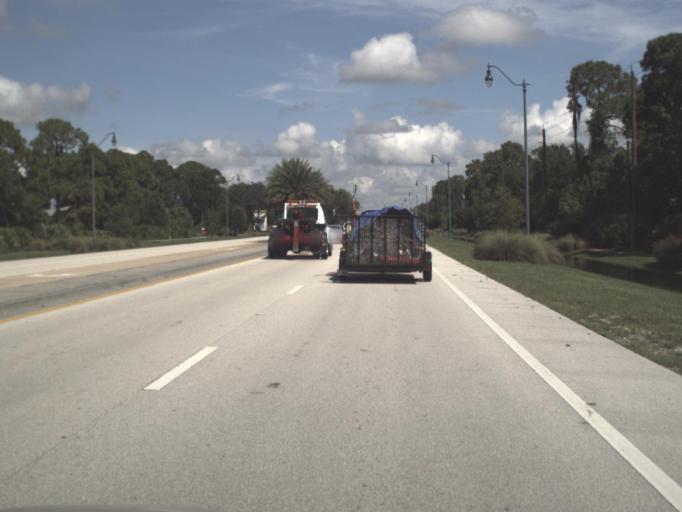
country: US
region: Florida
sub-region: Sarasota County
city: North Port
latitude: 27.0529
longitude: -82.1570
